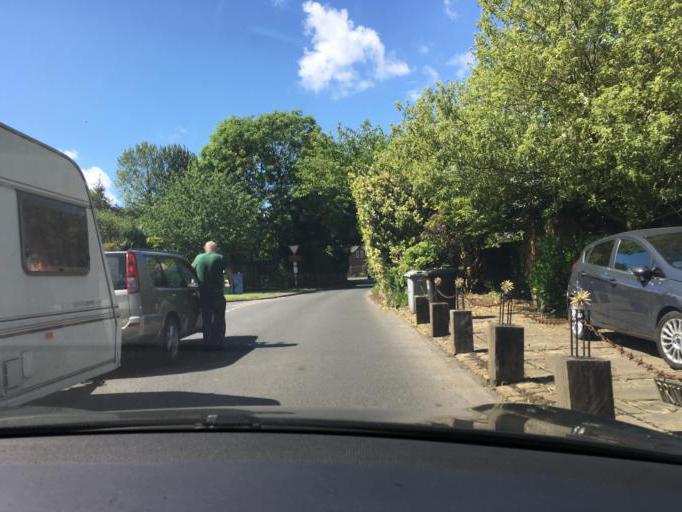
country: GB
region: England
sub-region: Cheshire East
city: Mobberley
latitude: 53.2877
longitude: -2.3351
